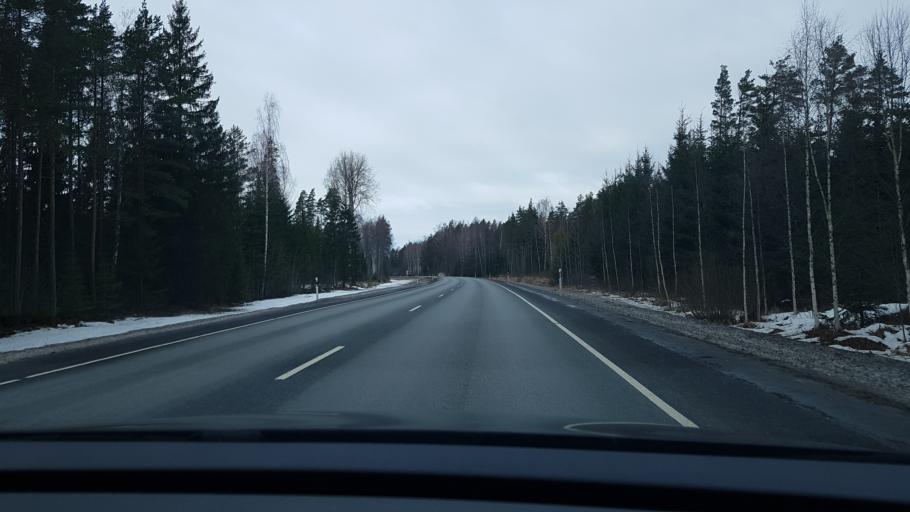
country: EE
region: Paernumaa
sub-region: Paikuse vald
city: Paikuse
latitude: 58.2537
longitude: 24.6822
